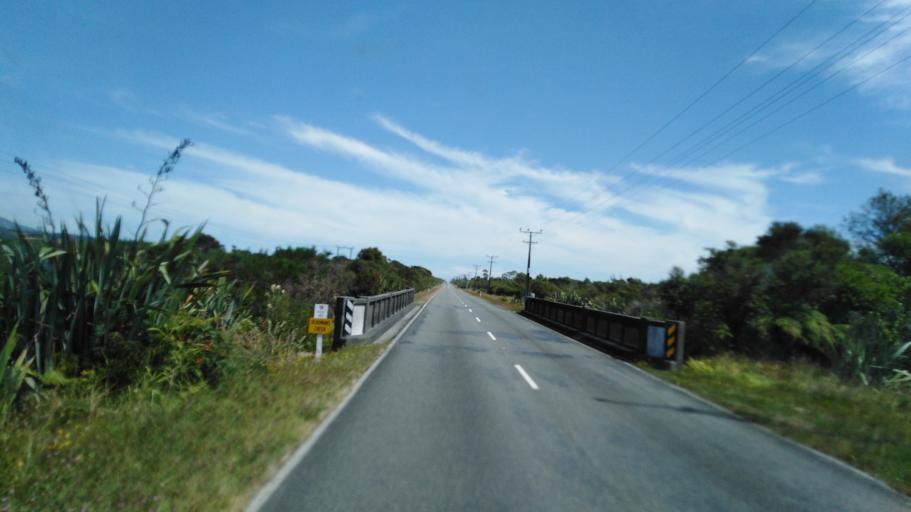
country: NZ
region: West Coast
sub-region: Buller District
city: Westport
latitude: -41.7448
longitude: 171.6868
